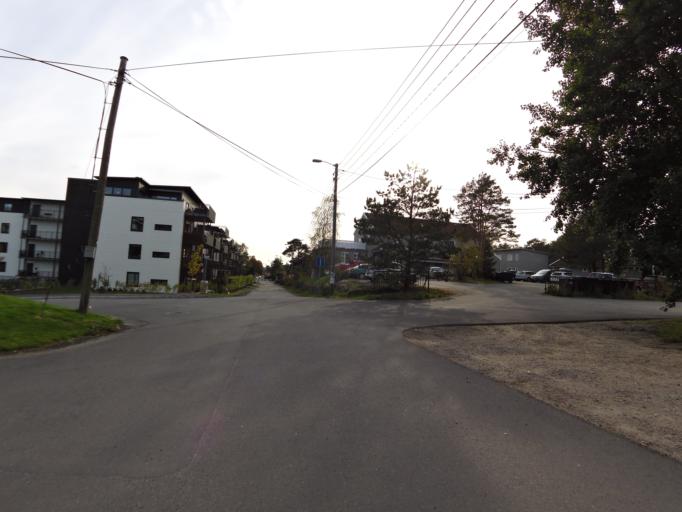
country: NO
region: Ostfold
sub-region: Fredrikstad
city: Fredrikstad
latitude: 59.2284
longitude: 10.9506
